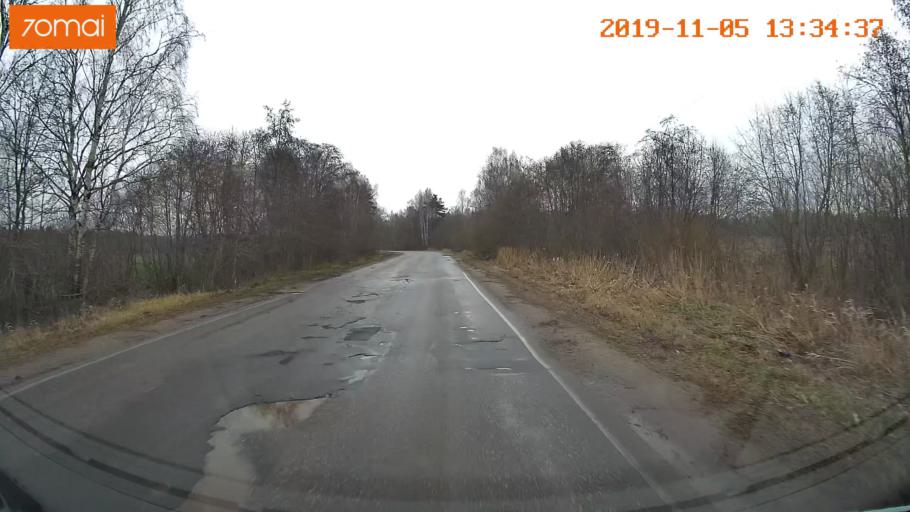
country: RU
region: Ivanovo
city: Shuya
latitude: 56.9021
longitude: 41.3899
